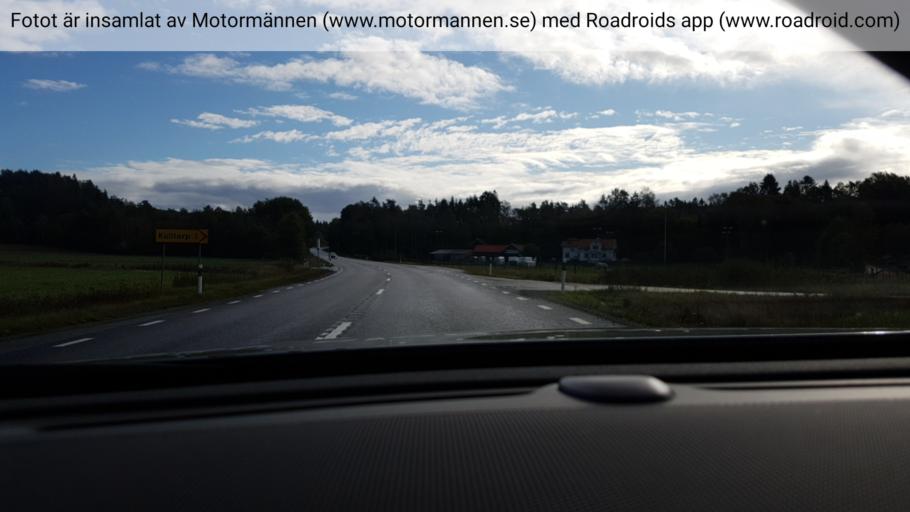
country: SE
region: Vaestra Goetaland
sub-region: Harryda Kommun
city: Ravlanda
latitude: 57.5851
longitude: 12.4722
